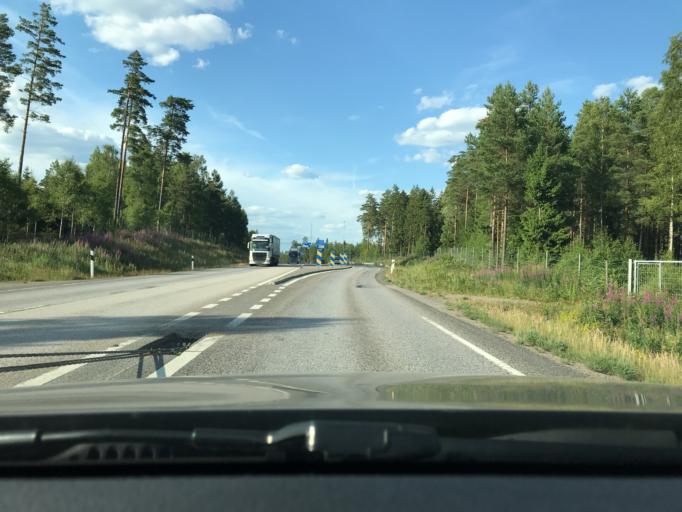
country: SE
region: Kronoberg
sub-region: Vaxjo Kommun
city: Braas
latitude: 57.0148
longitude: 15.0521
